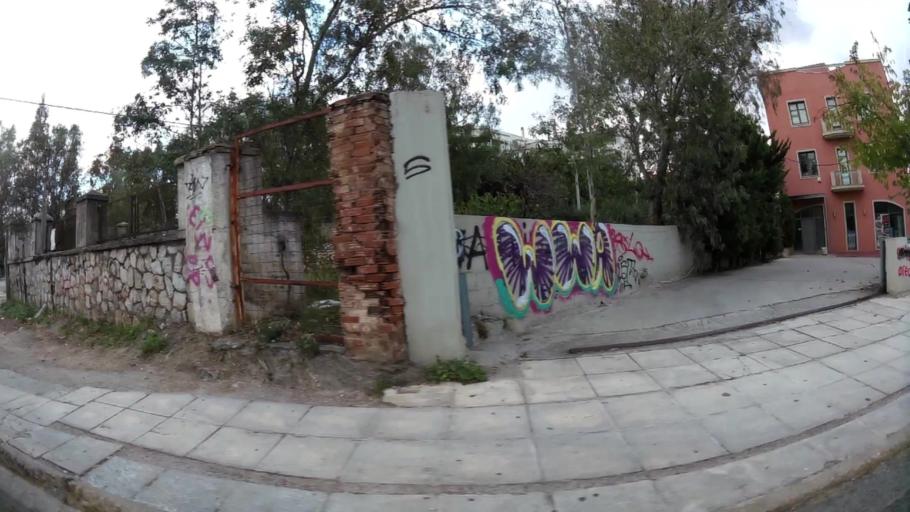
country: GR
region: Attica
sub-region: Nomarchia Athinas
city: Melissia
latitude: 38.0512
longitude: 23.8395
